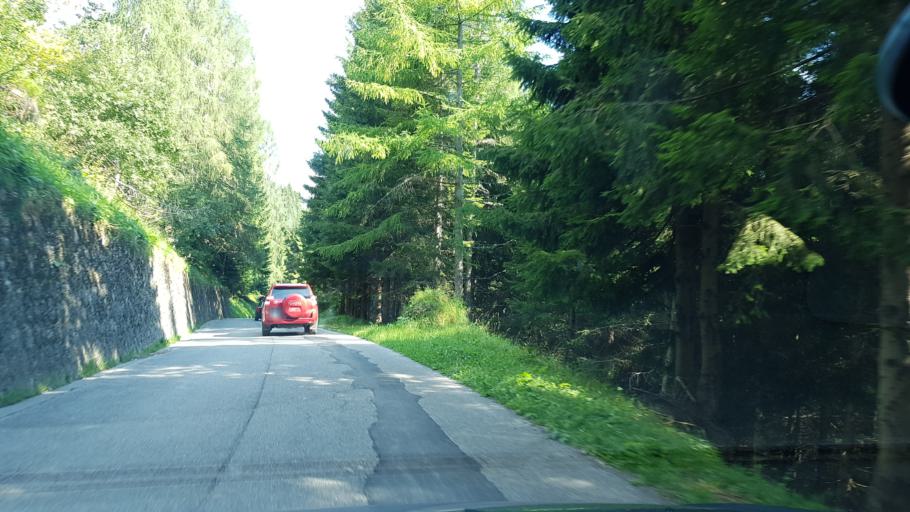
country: IT
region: Friuli Venezia Giulia
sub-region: Provincia di Udine
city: Sauris di Sotto
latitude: 46.4716
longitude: 12.6748
